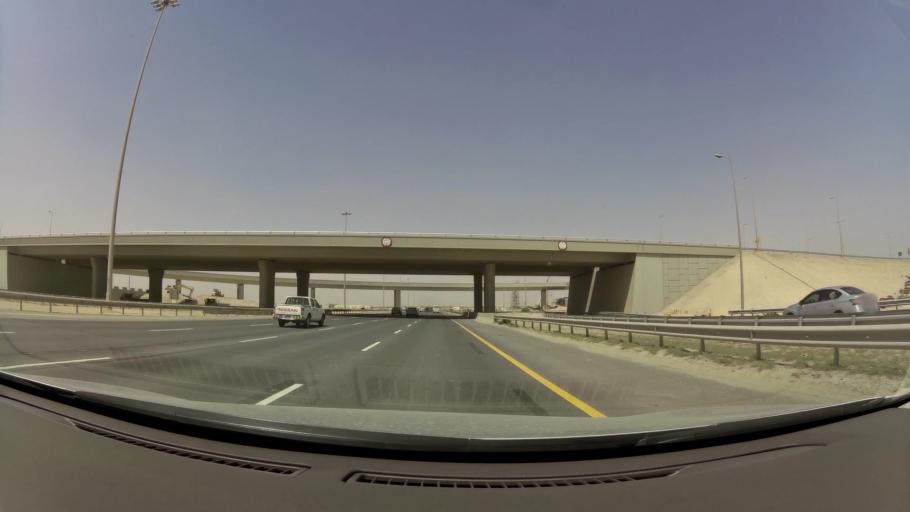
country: QA
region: Baladiyat Umm Salal
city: Umm Salal Muhammad
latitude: 25.4008
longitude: 51.4300
